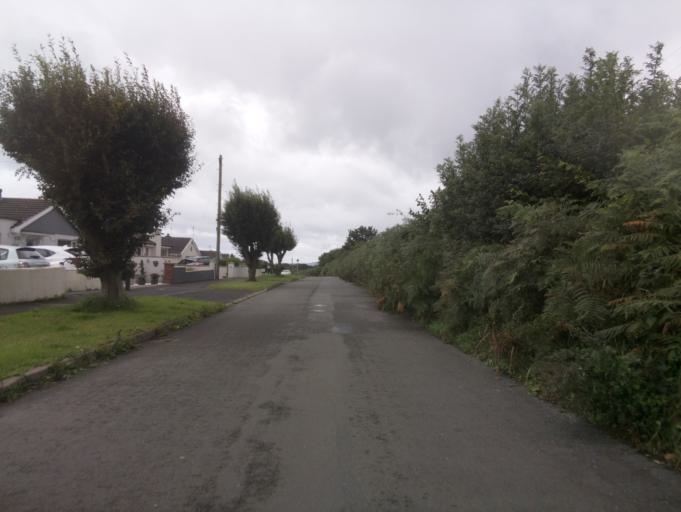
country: GB
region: England
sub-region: Devon
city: Dartmouth
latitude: 50.3304
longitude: -3.6000
